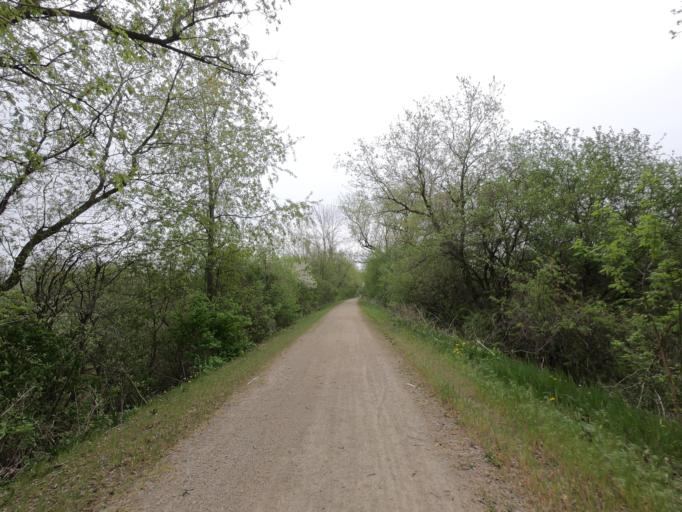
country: US
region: Wisconsin
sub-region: Jefferson County
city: Johnson Creek
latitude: 43.0371
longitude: -88.7657
